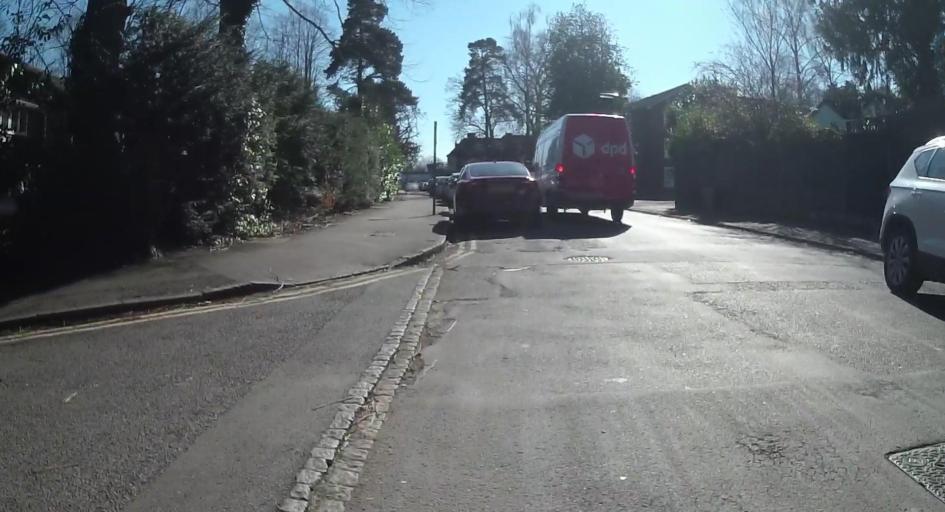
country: GB
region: England
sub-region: Surrey
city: Walton-on-Thames
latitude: 51.3747
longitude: -0.4155
